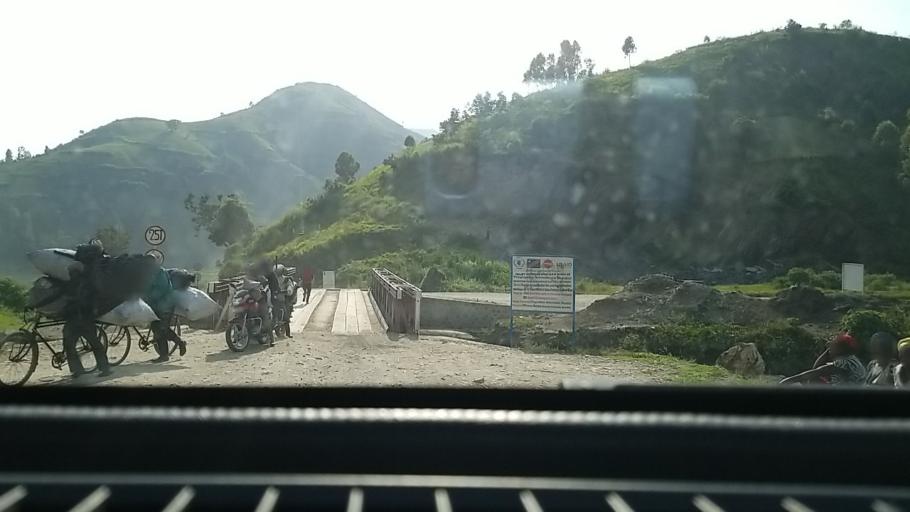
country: CD
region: Nord Kivu
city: Sake
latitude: -1.5715
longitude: 29.0470
